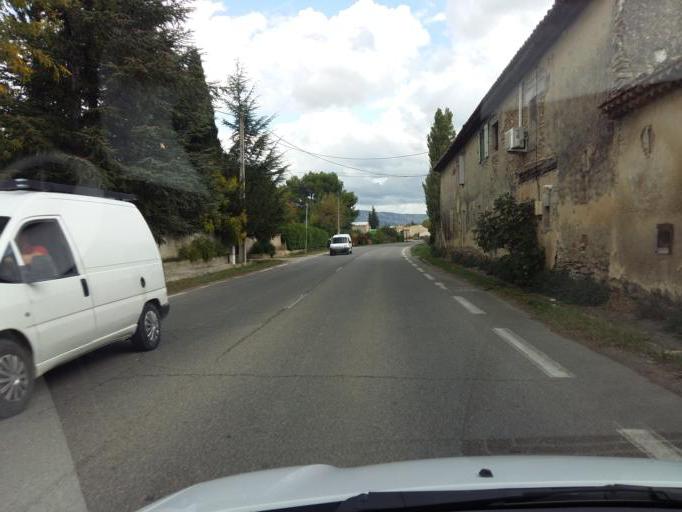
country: FR
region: Provence-Alpes-Cote d'Azur
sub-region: Departement du Vaucluse
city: L'Isle-sur-la-Sorgue
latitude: 43.9126
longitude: 5.0373
